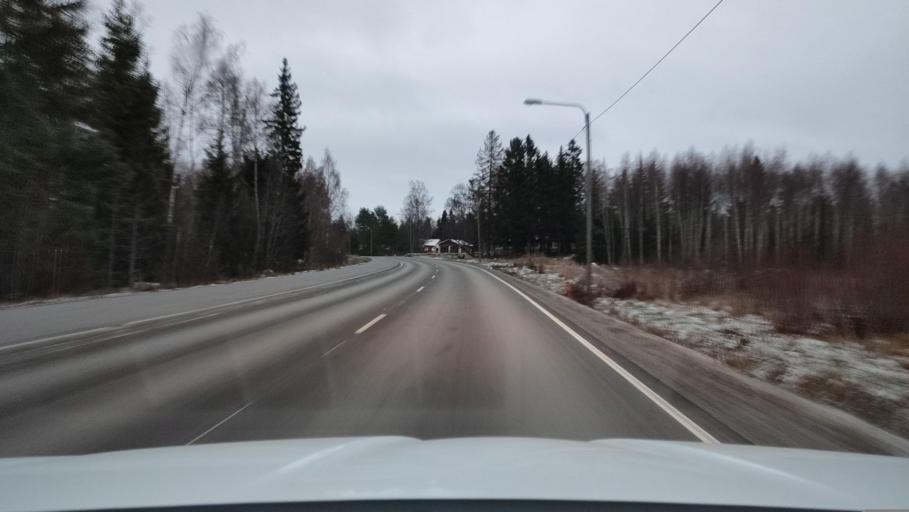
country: FI
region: Ostrobothnia
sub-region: Vaasa
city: Replot
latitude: 63.2210
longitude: 21.4150
